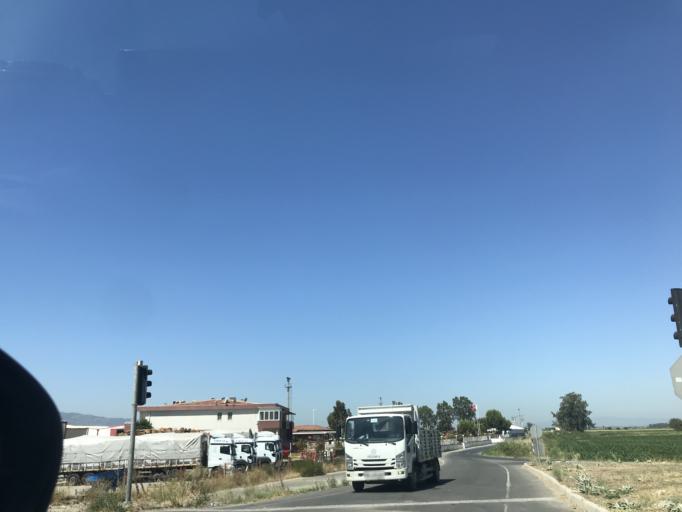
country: TR
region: Aydin
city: Tepecik
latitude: 37.7981
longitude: 27.8391
